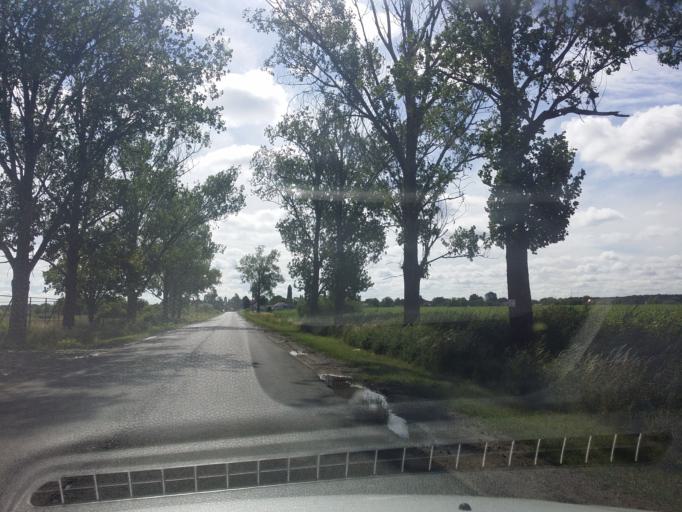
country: HU
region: Jasz-Nagykun-Szolnok
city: Jaszszentandras
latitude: 47.6447
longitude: 20.1732
